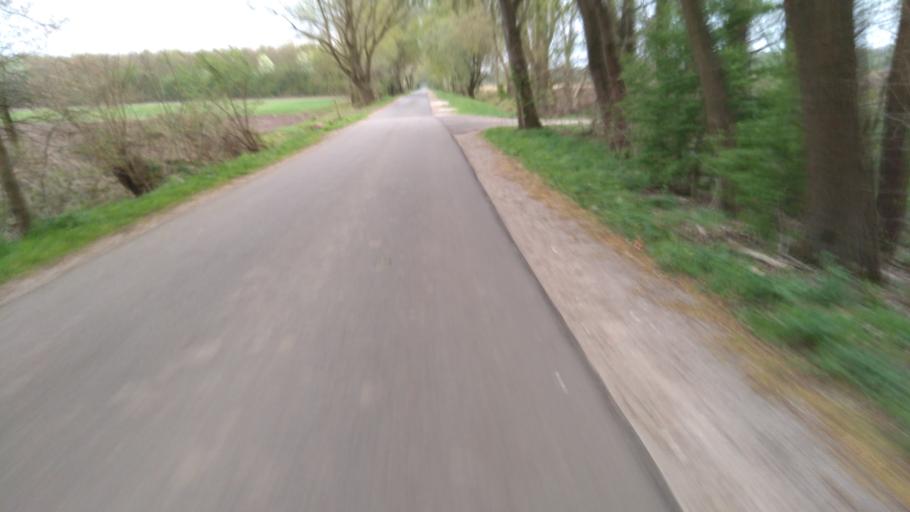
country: DE
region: Lower Saxony
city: Bliedersdorf
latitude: 53.4401
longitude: 9.5580
